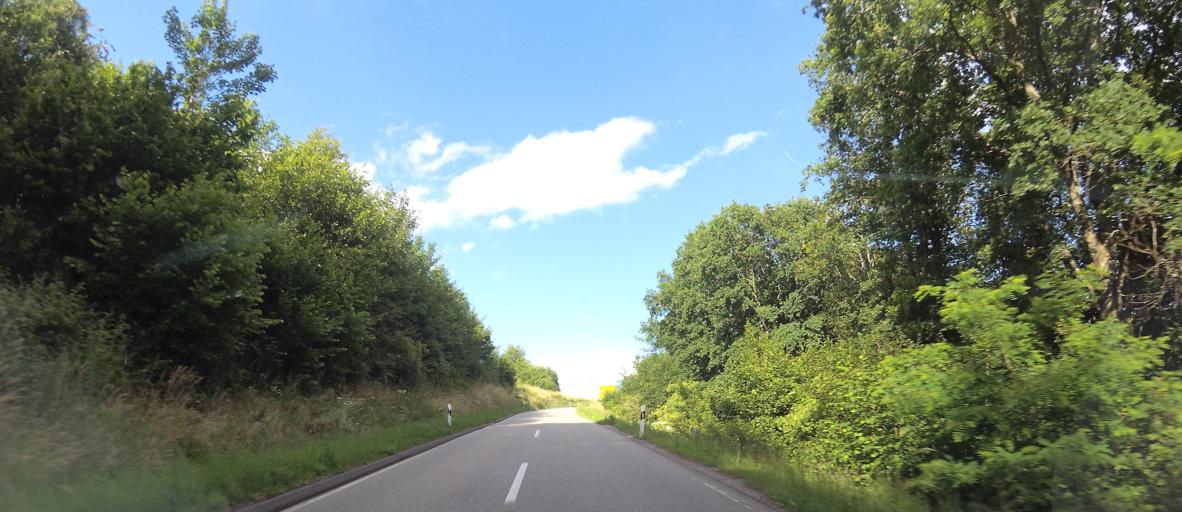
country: DE
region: Rheinland-Pfalz
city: Vinningen
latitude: 49.1503
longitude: 7.5626
